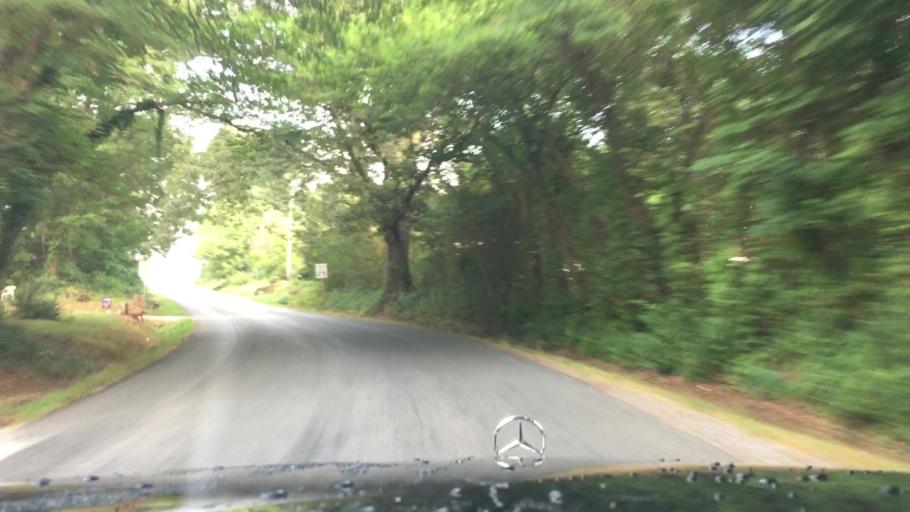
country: US
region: Virginia
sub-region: Campbell County
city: Altavista
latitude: 37.1480
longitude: -79.2932
